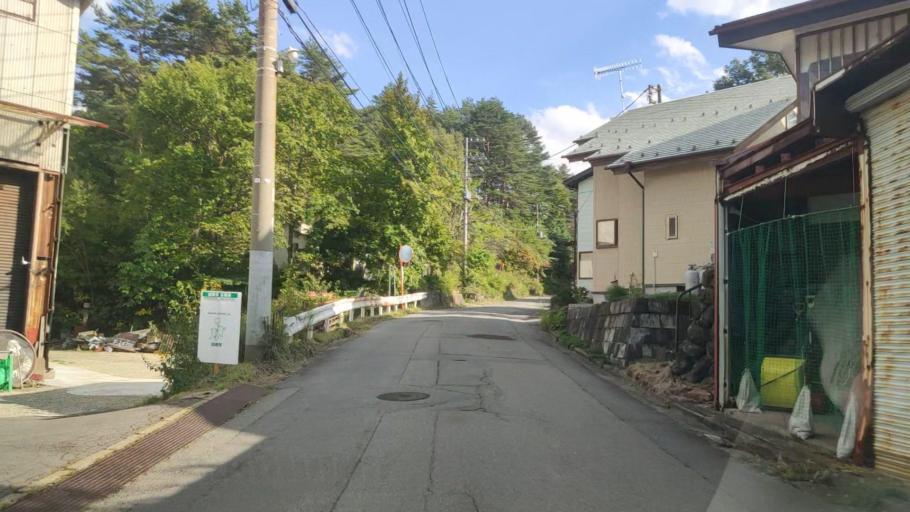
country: JP
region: Gunma
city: Nakanojomachi
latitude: 36.6204
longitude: 138.6096
